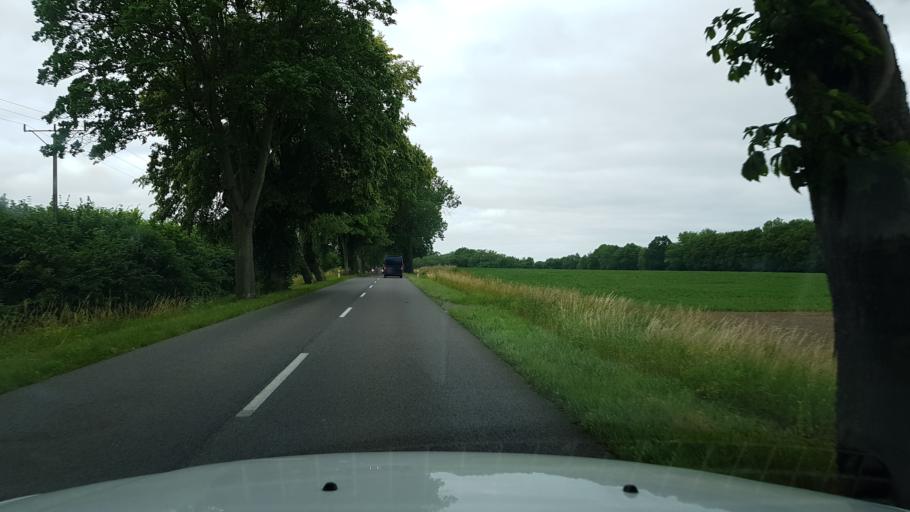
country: PL
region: West Pomeranian Voivodeship
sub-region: Powiat kamienski
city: Kamien Pomorski
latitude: 53.9609
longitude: 14.8032
